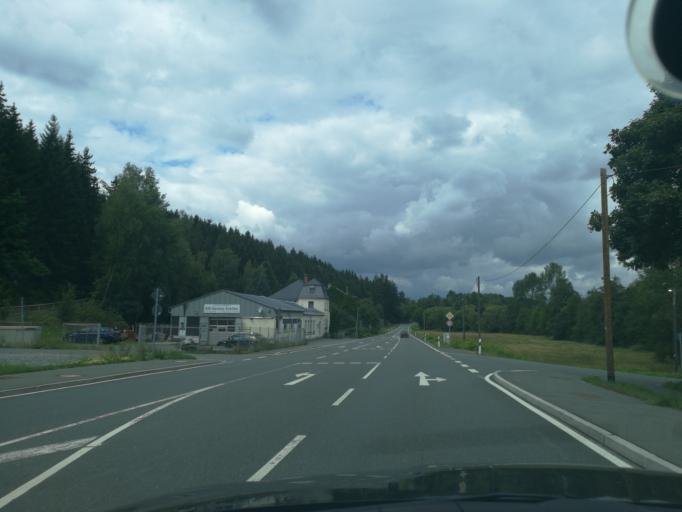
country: DE
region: Saxony
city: Adorf
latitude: 50.3435
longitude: 12.2422
